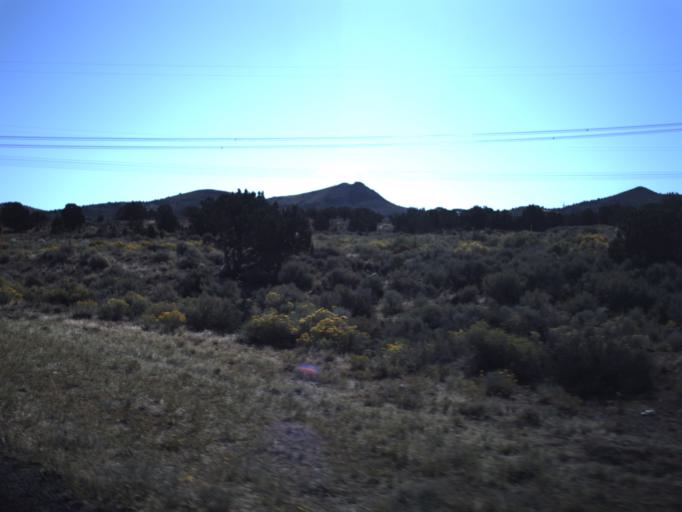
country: US
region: Utah
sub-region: Washington County
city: Enterprise
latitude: 37.6739
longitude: -113.5315
